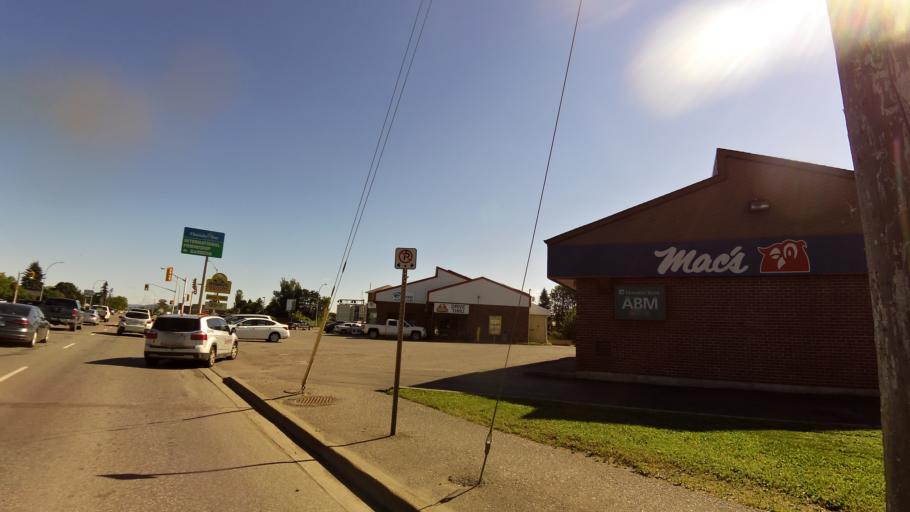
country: CA
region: Ontario
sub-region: Thunder Bay District
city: Thunder Bay
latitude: 48.3835
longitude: -89.2633
